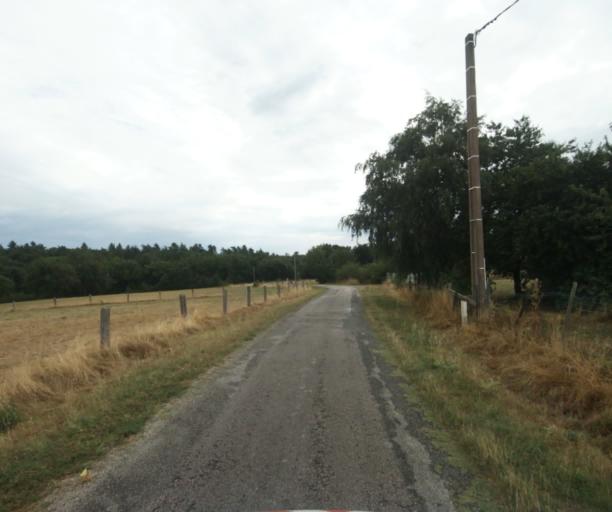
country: FR
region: Midi-Pyrenees
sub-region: Departement de la Haute-Garonne
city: Revel
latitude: 43.4274
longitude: 1.9919
